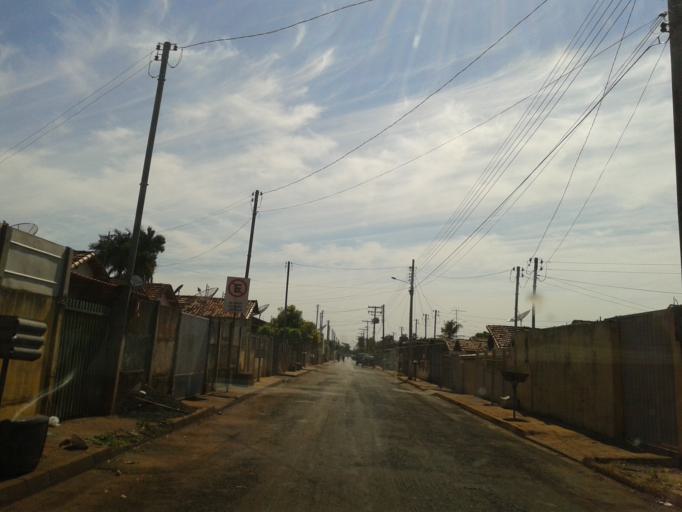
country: BR
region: Minas Gerais
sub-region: Santa Vitoria
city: Santa Vitoria
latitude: -19.0023
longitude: -50.5508
